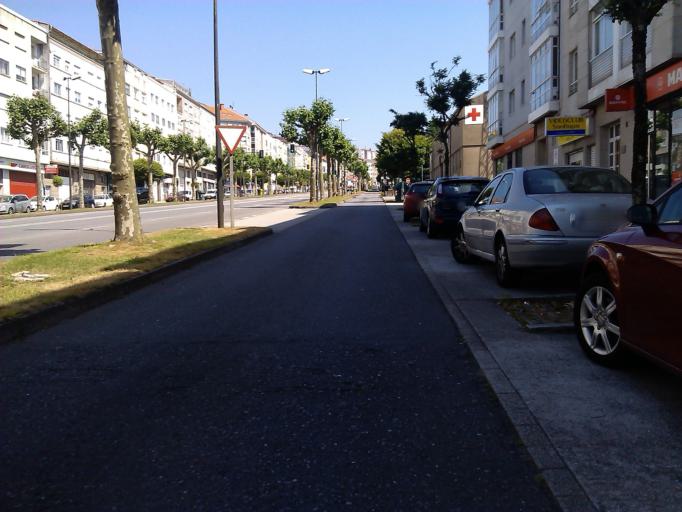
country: ES
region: Galicia
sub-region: Provincia da Coruna
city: Santiago de Compostela
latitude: 42.8813
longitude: -8.5330
